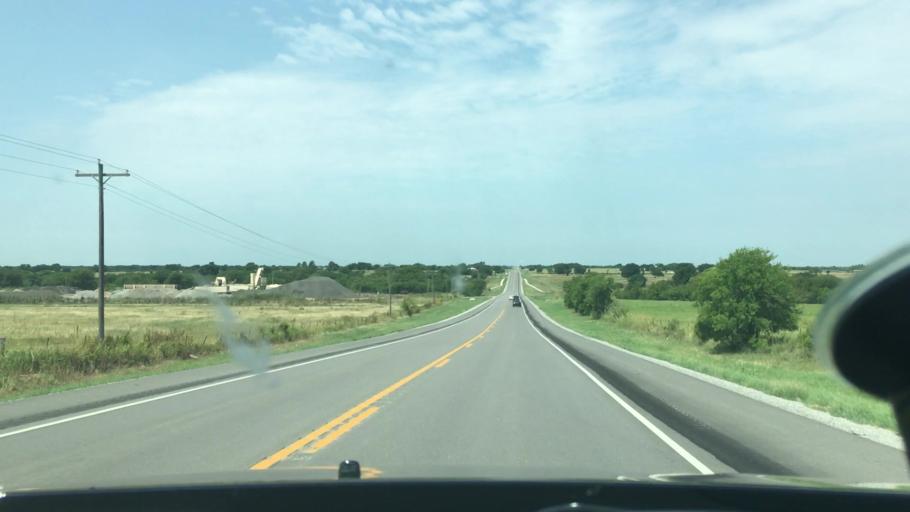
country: US
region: Oklahoma
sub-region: Love County
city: Marietta
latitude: 33.9404
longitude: -97.1734
